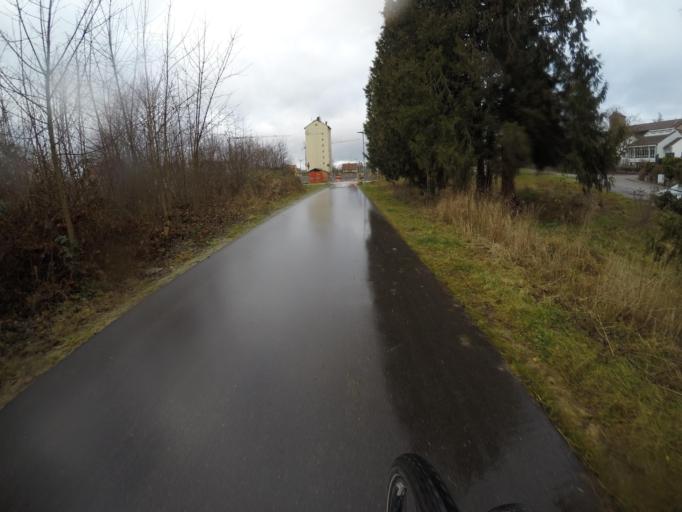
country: DE
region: Baden-Wuerttemberg
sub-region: Regierungsbezirk Stuttgart
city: Vaihingen an der Enz
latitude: 48.9318
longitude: 8.9652
